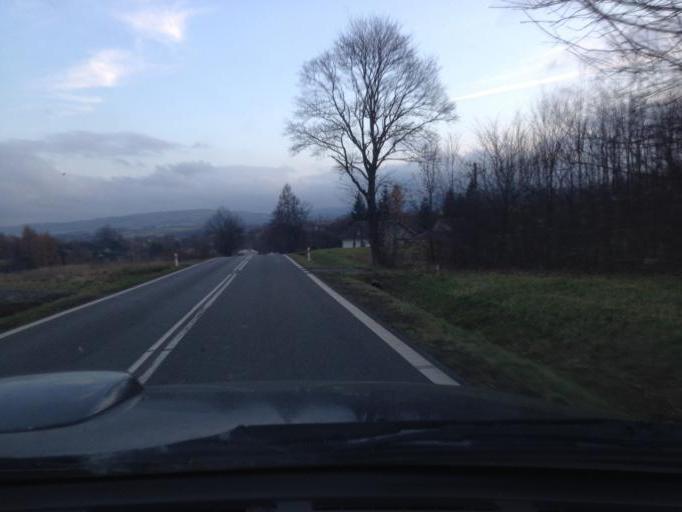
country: PL
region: Subcarpathian Voivodeship
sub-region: Powiat jasielski
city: Nowy Zmigrod
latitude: 49.6262
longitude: 21.5343
